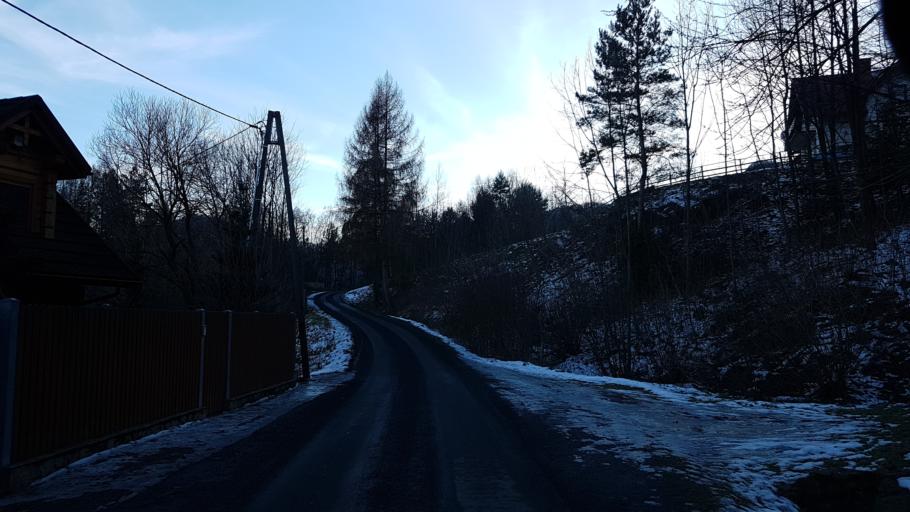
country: PL
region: Lesser Poland Voivodeship
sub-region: Powiat nowosadecki
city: Rytro
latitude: 49.4905
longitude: 20.6571
